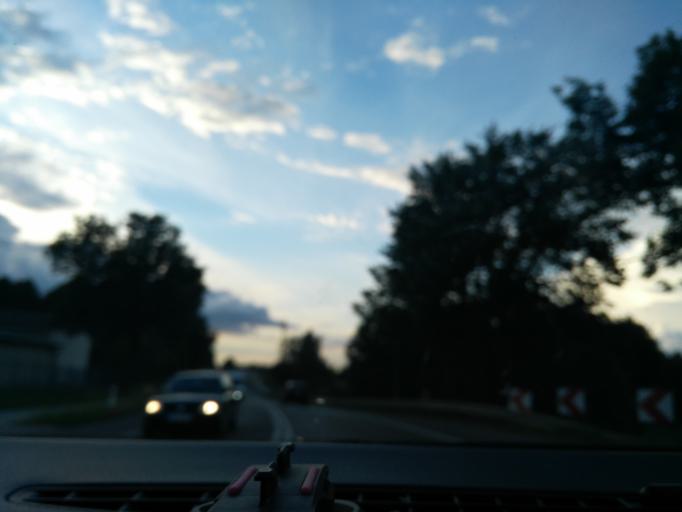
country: PL
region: Lublin Voivodeship
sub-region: Powiat lubartowski
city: Serniki
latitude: 51.4196
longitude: 22.6421
